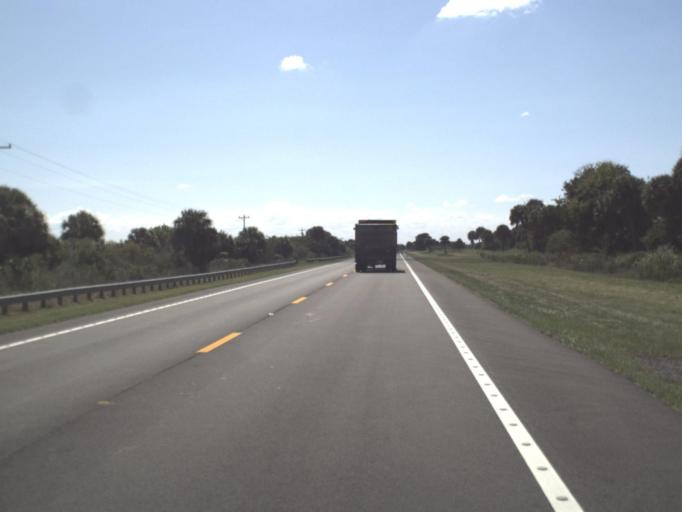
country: US
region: Florida
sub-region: Glades County
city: Buckhead Ridge
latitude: 27.0519
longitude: -80.9855
